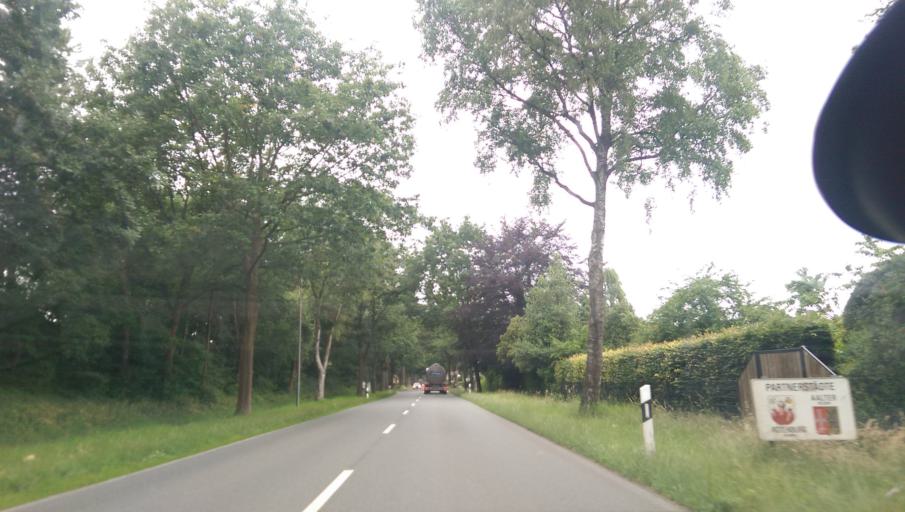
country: DE
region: Lower Saxony
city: Rotenburg
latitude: 53.0978
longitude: 9.4044
